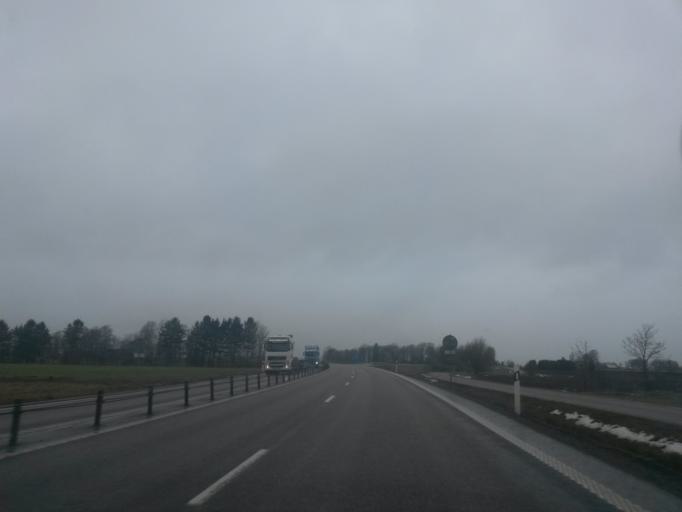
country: SE
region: Vaestra Goetaland
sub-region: Vanersborgs Kommun
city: Vargon
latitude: 58.2925
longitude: 12.3896
